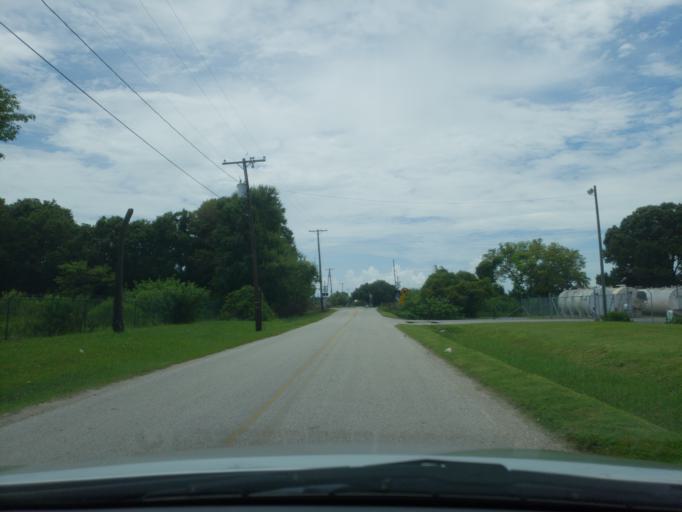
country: US
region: Florida
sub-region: Hillsborough County
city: Palm River-Clair Mel
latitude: 27.9193
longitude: -82.3966
